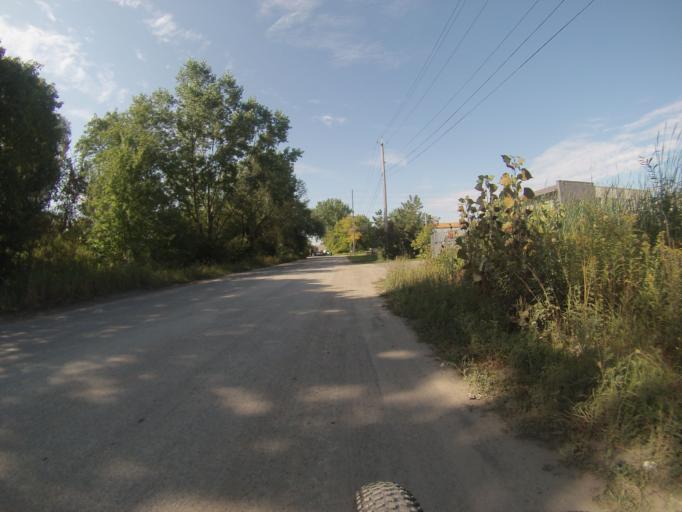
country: CA
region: Ontario
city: Ottawa
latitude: 45.3648
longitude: -75.6480
